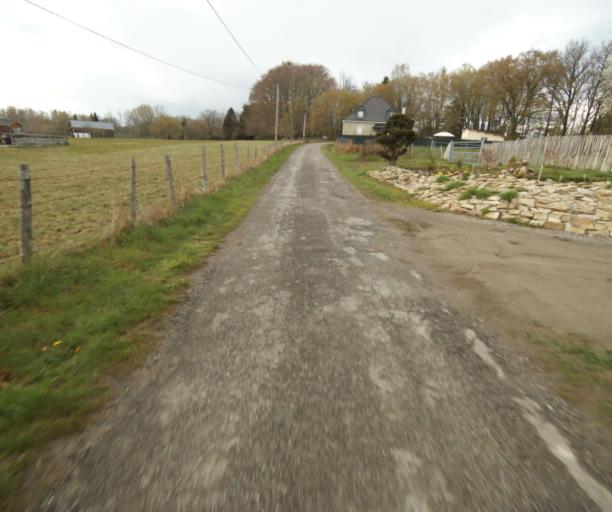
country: FR
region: Limousin
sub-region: Departement de la Correze
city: Saint-Privat
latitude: 45.2160
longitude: 2.0195
